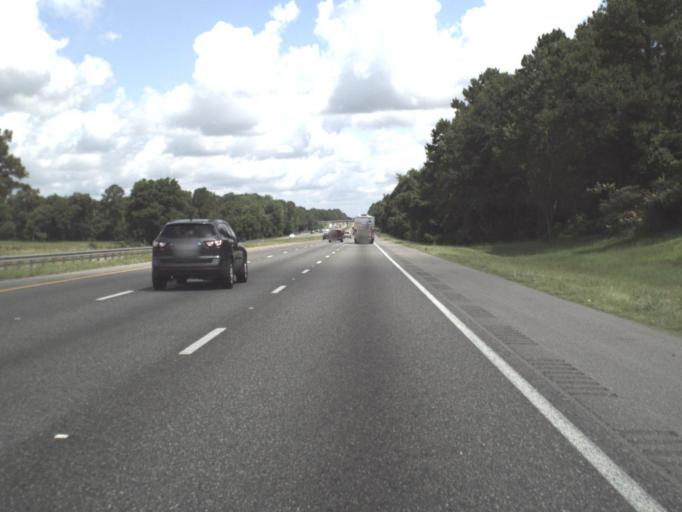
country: US
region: Florida
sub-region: Columbia County
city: Lake City
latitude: 30.0835
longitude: -82.6359
